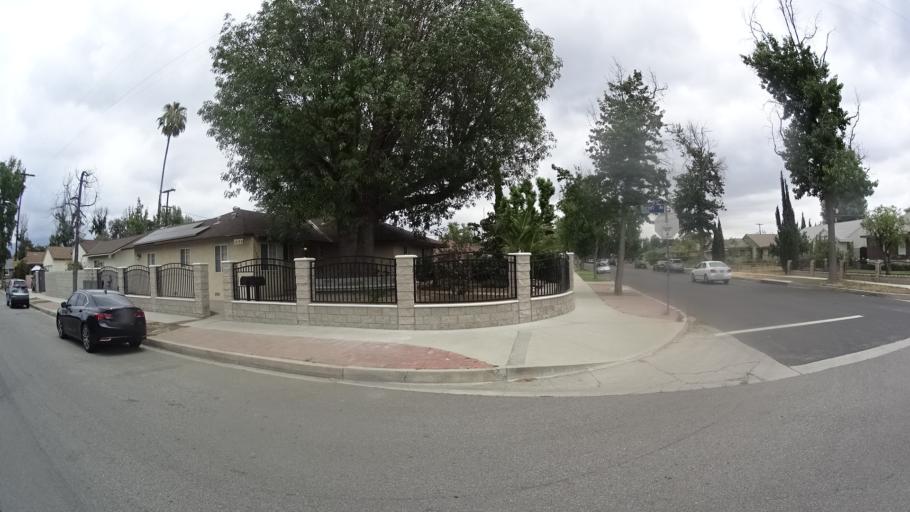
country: US
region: California
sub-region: Los Angeles County
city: San Fernando
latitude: 34.2583
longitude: -118.4631
